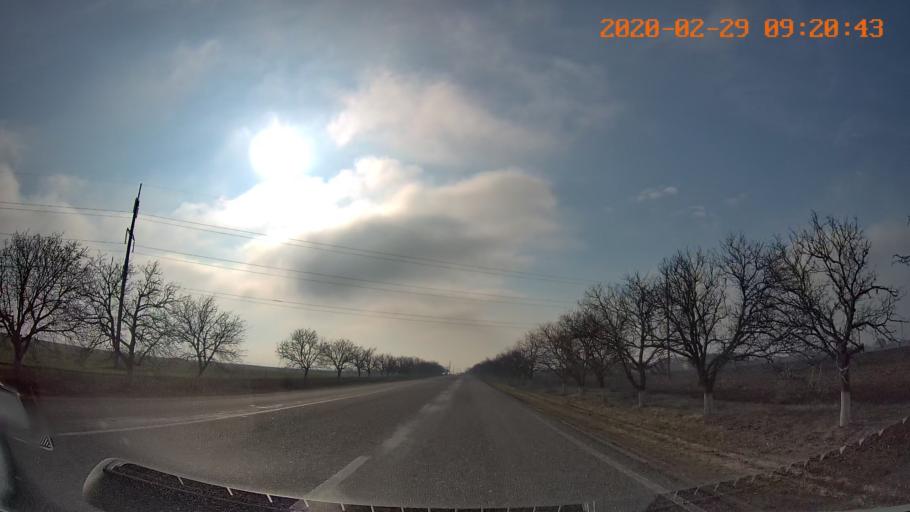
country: MD
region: Telenesti
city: Pervomaisc
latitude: 46.7450
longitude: 29.9516
